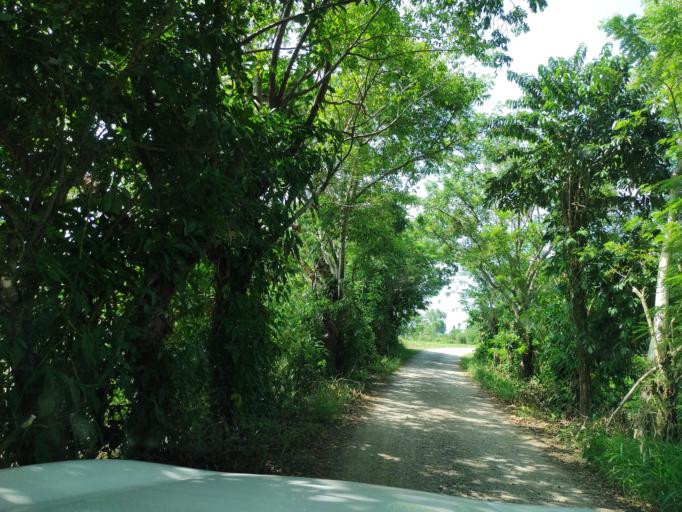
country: MX
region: Veracruz
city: Martinez de la Torre
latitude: 20.0905
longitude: -97.0470
